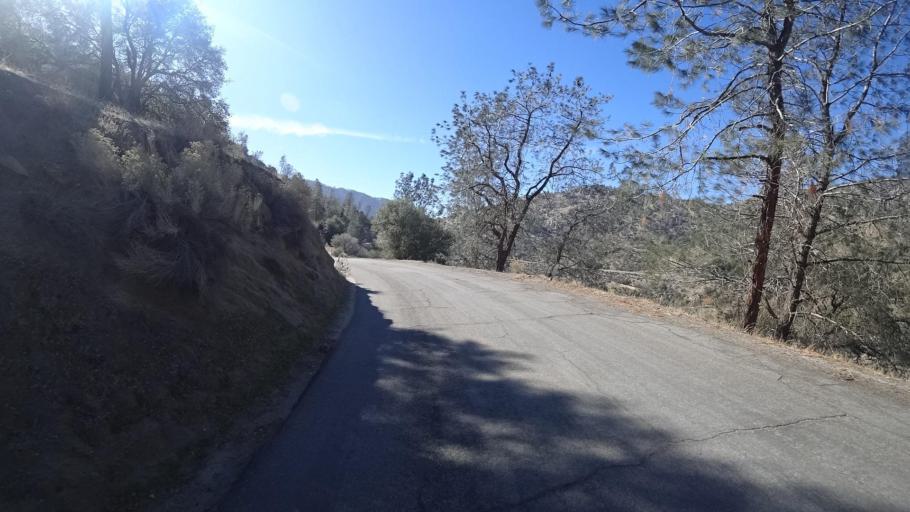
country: US
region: California
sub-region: Kern County
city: Bodfish
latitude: 35.5655
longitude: -118.5811
